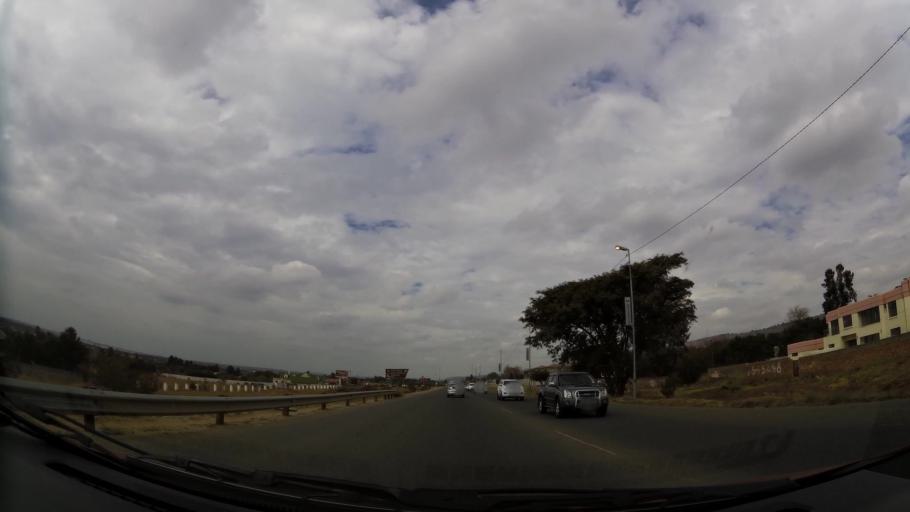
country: ZA
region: Gauteng
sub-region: West Rand District Municipality
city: Muldersdriseloop
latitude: -26.0764
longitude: 27.8565
